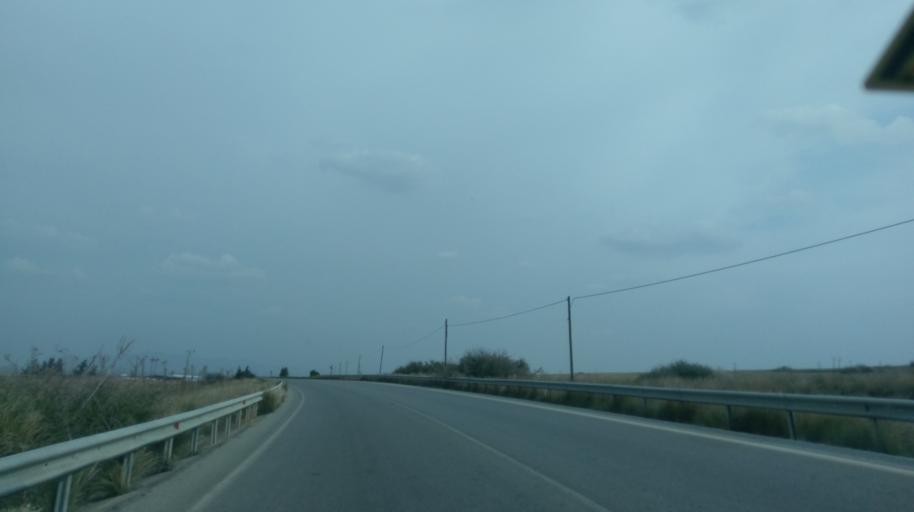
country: CY
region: Ammochostos
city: Lefkonoiko
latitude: 35.2522
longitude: 33.6302
